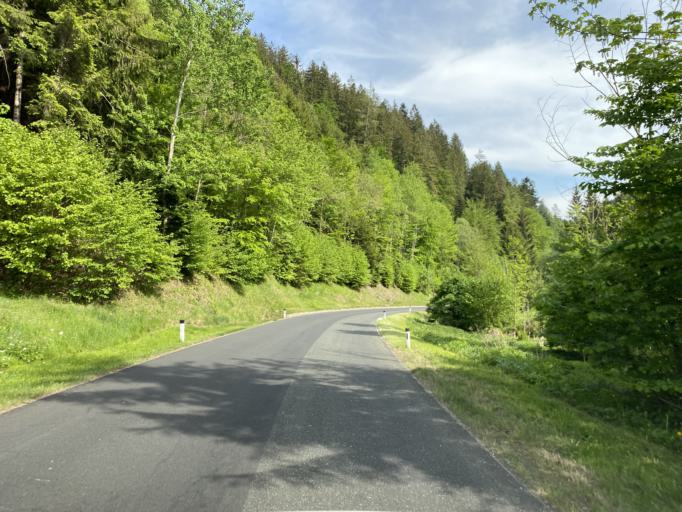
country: AT
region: Styria
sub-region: Politischer Bezirk Weiz
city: Koglhof
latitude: 47.3233
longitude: 15.6349
